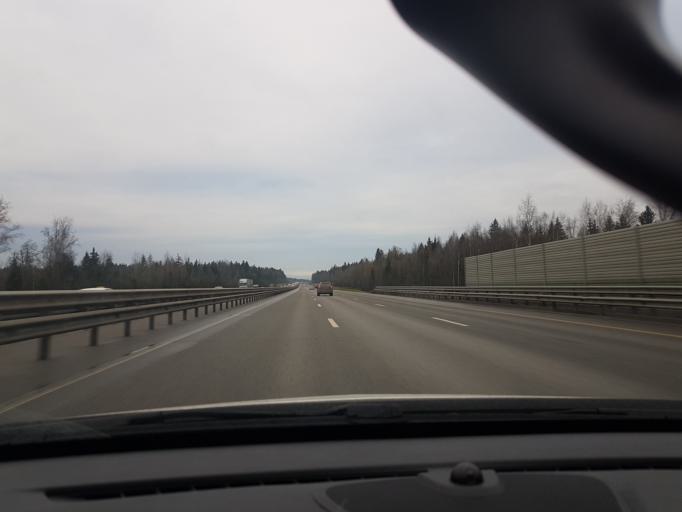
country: RU
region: Moskovskaya
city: Kostrovo
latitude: 55.8609
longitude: 36.7428
